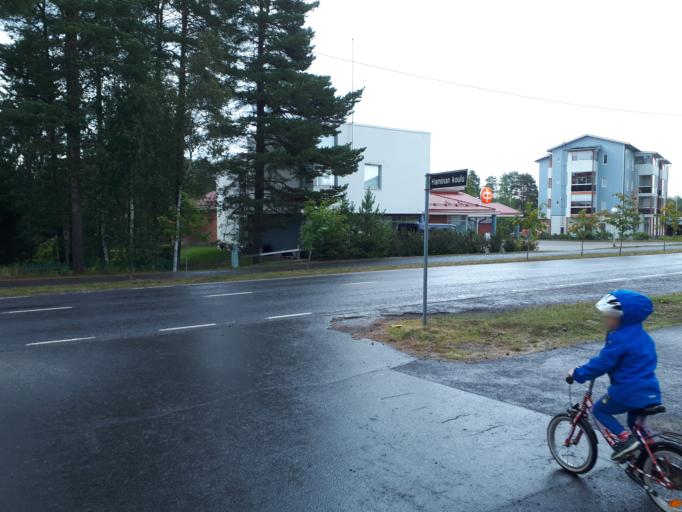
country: FI
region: Northern Ostrobothnia
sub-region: Oulunkaari
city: Ii
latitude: 65.3227
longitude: 25.3733
